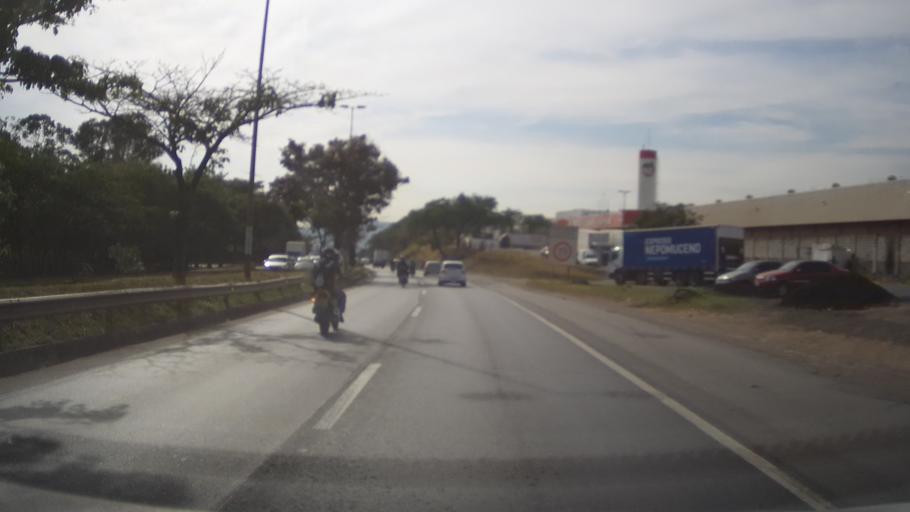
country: BR
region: Minas Gerais
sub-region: Contagem
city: Contagem
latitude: -19.9223
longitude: -44.0218
